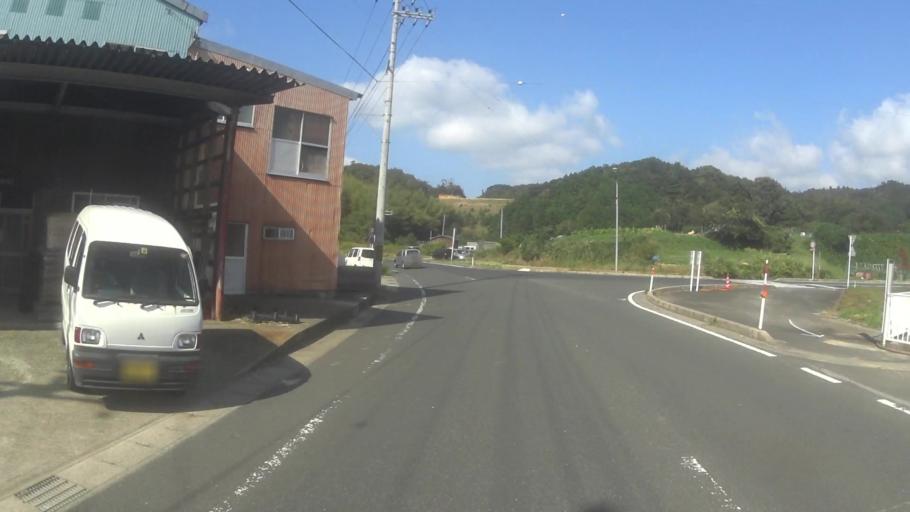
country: JP
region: Kyoto
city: Miyazu
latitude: 35.6882
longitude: 135.0522
